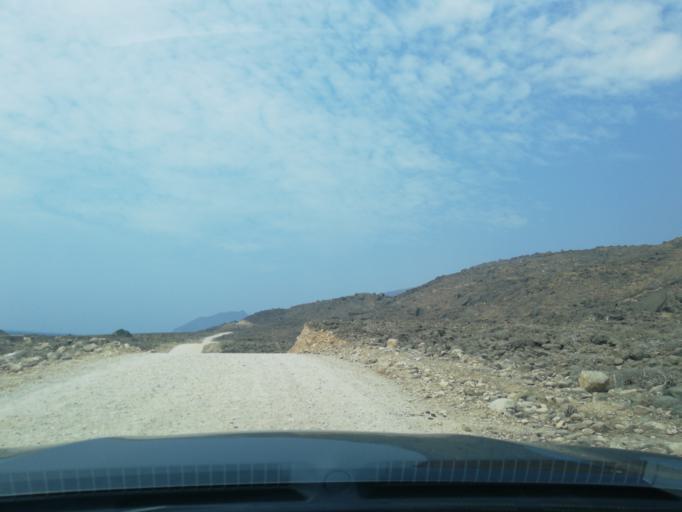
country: OM
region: Zufar
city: Salalah
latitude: 16.8248
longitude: 53.6996
